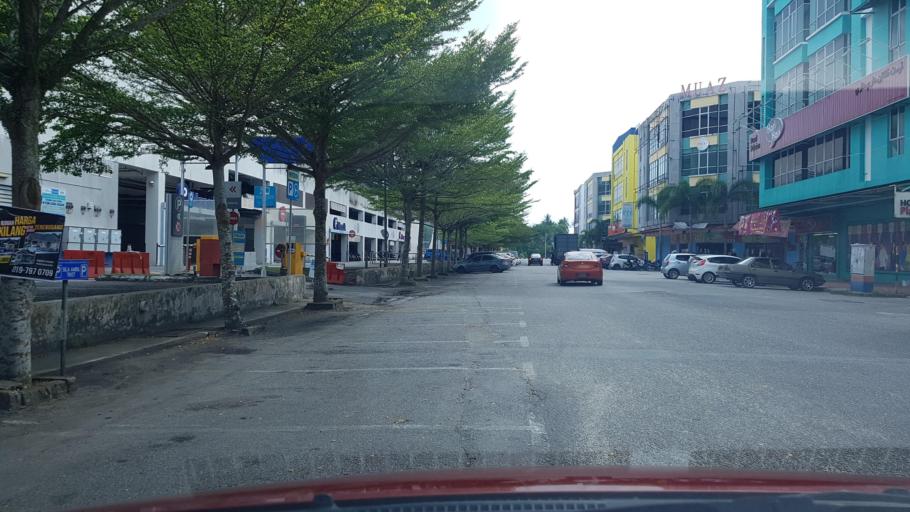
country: MY
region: Terengganu
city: Kuala Terengganu
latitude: 5.3563
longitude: 103.0969
